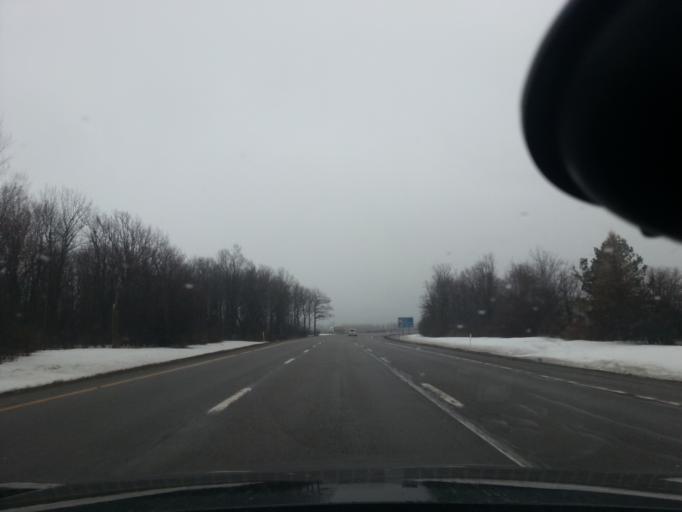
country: US
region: New York
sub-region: Jefferson County
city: Watertown
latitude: 44.0110
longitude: -75.9131
